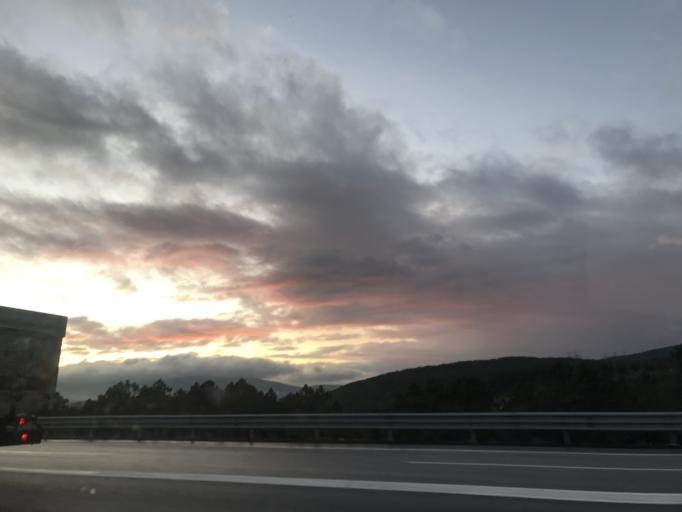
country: TR
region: Istanbul
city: Sultanbeyli
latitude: 40.9612
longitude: 29.3197
